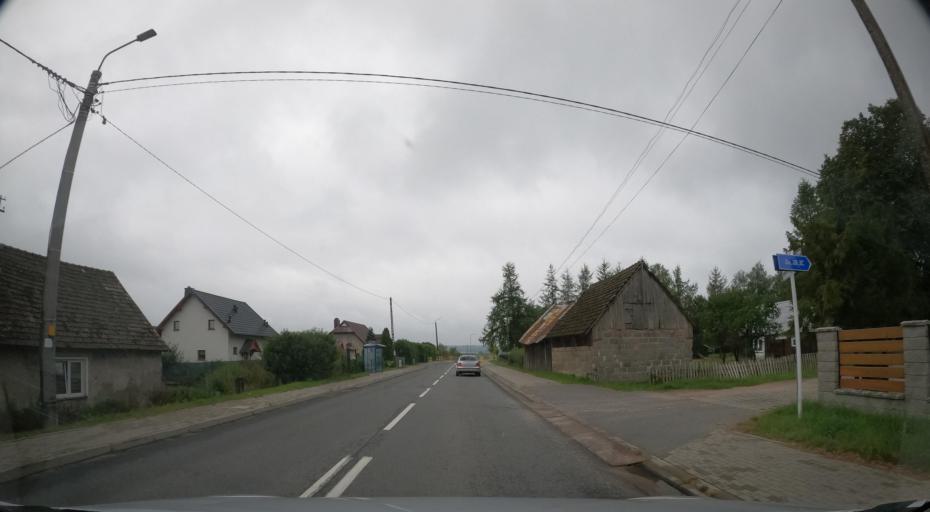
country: PL
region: Pomeranian Voivodeship
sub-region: Powiat wejherowski
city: Linia
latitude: 54.4792
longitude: 17.8561
